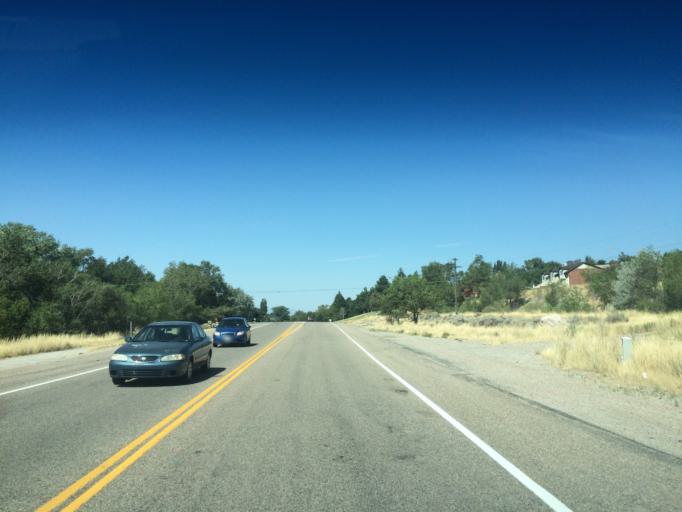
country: US
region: Utah
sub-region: Weber County
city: Ogden
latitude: 41.2390
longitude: -111.9319
